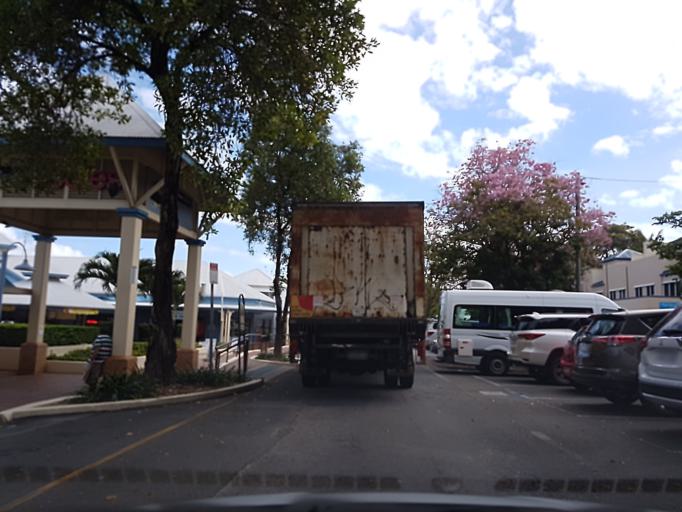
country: AU
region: Queensland
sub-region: Cairns
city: Port Douglas
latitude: -16.4819
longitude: 145.4634
